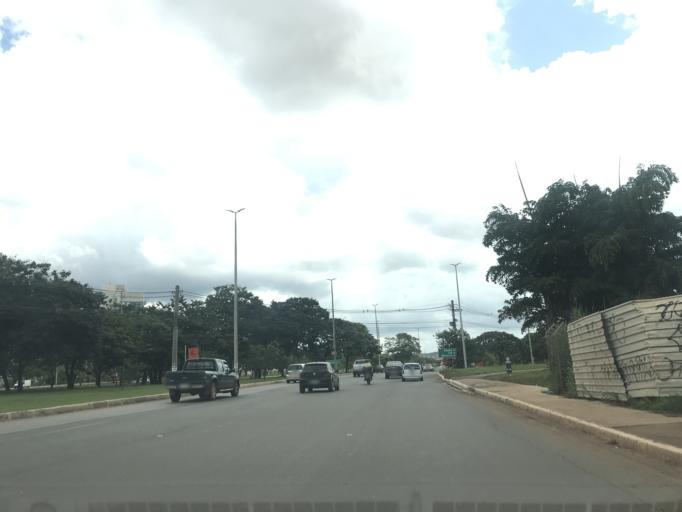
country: BR
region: Federal District
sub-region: Brasilia
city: Brasilia
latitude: -15.8352
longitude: -48.0489
